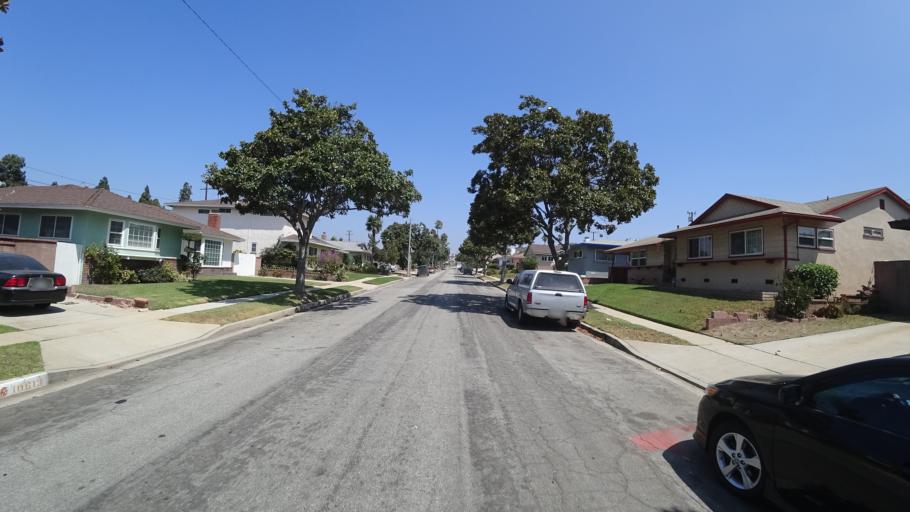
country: US
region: California
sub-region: Los Angeles County
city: Westmont
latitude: 33.9395
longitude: -118.3253
